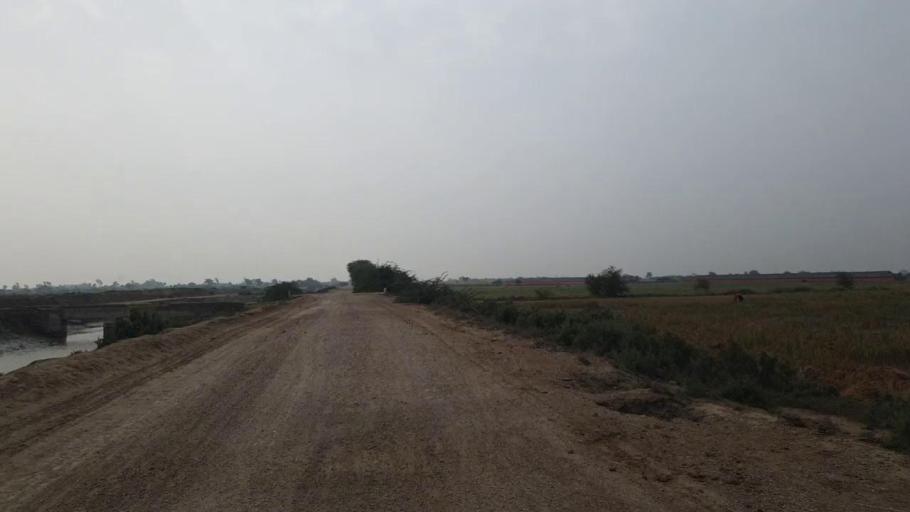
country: PK
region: Sindh
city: Kario
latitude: 24.8917
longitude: 68.5262
